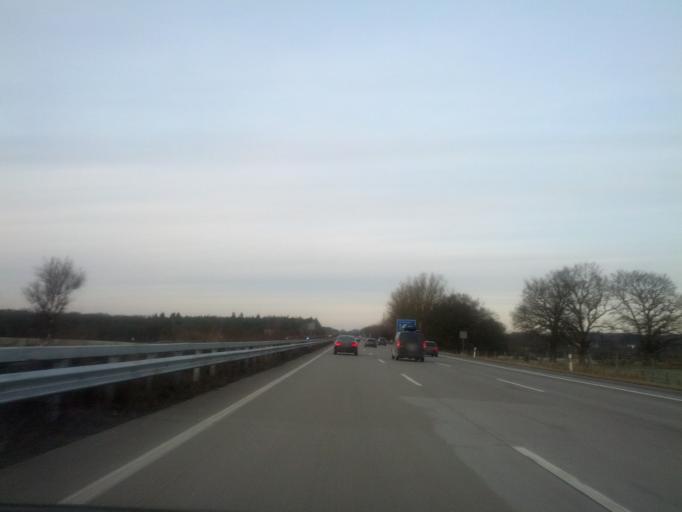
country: DE
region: Lower Saxony
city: Brackel
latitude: 53.2972
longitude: 10.0754
